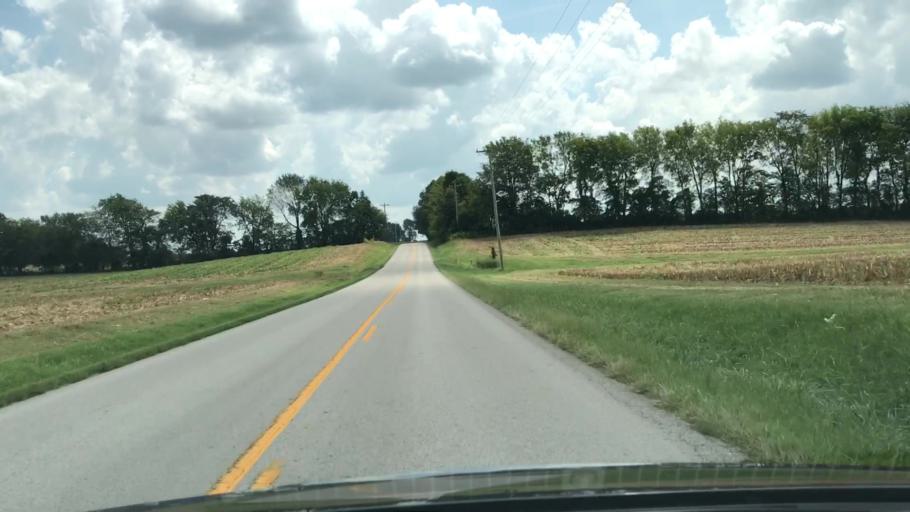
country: US
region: Kentucky
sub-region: Todd County
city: Elkton
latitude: 36.7838
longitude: -87.1268
